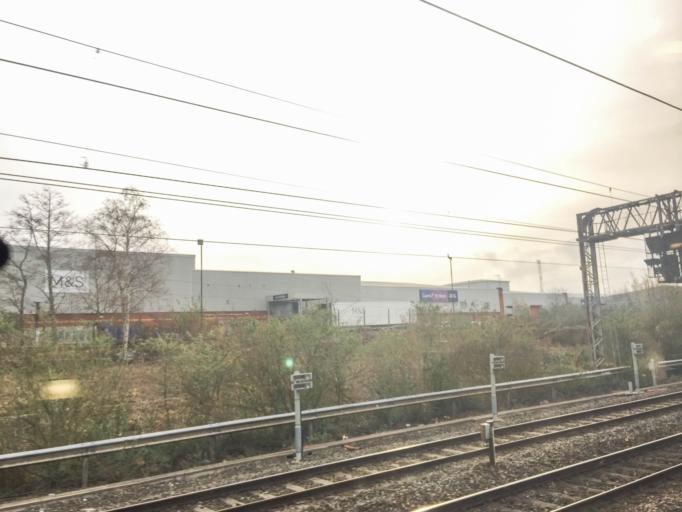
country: GB
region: England
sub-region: Cheshire East
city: Crewe
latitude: 53.0961
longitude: -2.4363
